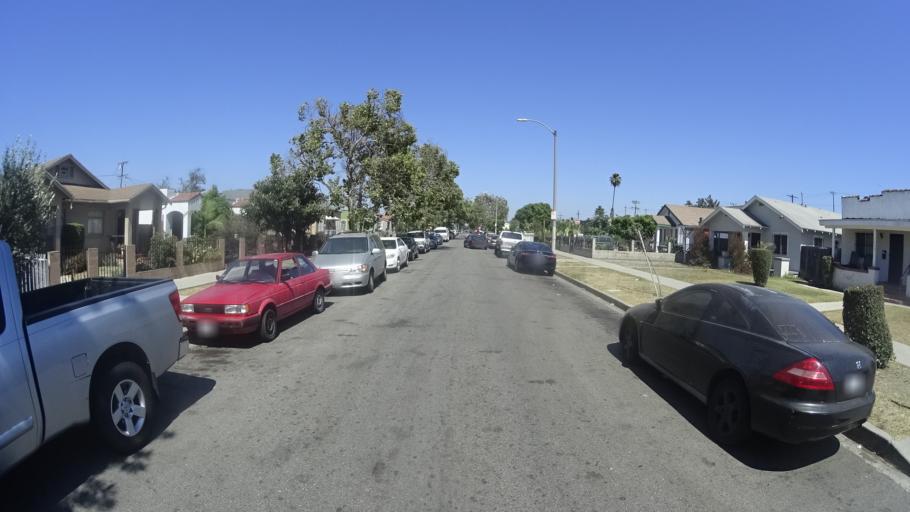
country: US
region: California
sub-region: Los Angeles County
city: View Park-Windsor Hills
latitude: 33.9941
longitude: -118.3022
